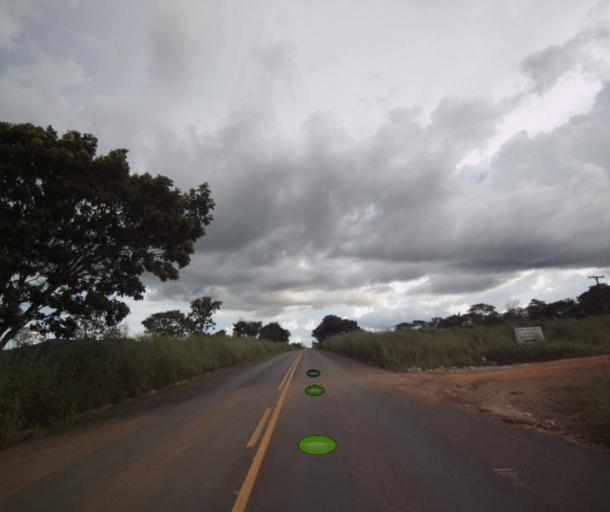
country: BR
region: Goias
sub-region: Niquelandia
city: Niquelandia
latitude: -14.4927
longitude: -48.4911
